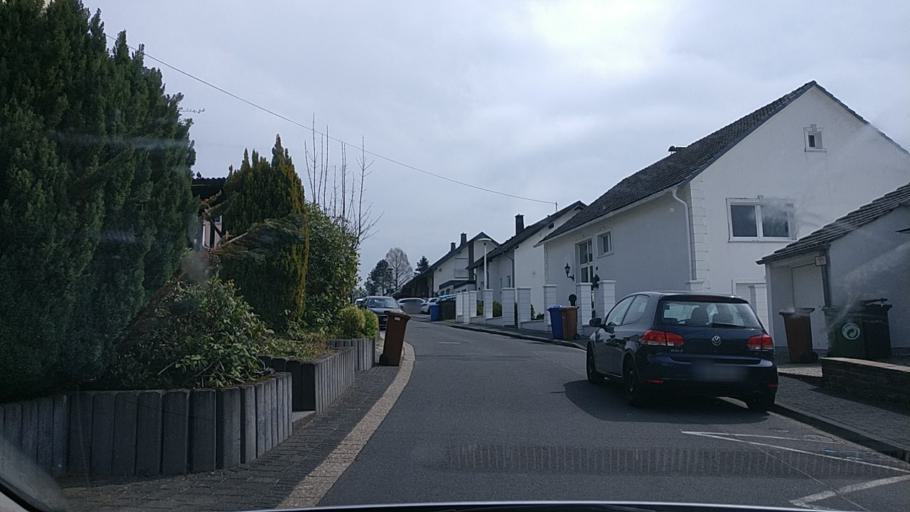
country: DE
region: Rheinland-Pfalz
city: Peterslahr
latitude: 50.6258
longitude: 7.4316
